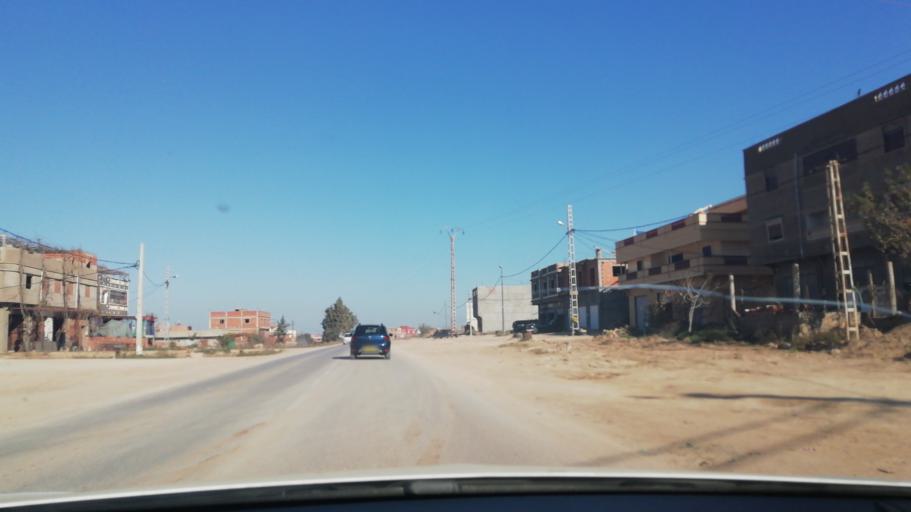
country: DZ
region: Tlemcen
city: Nedroma
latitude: 35.0102
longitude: -1.8998
